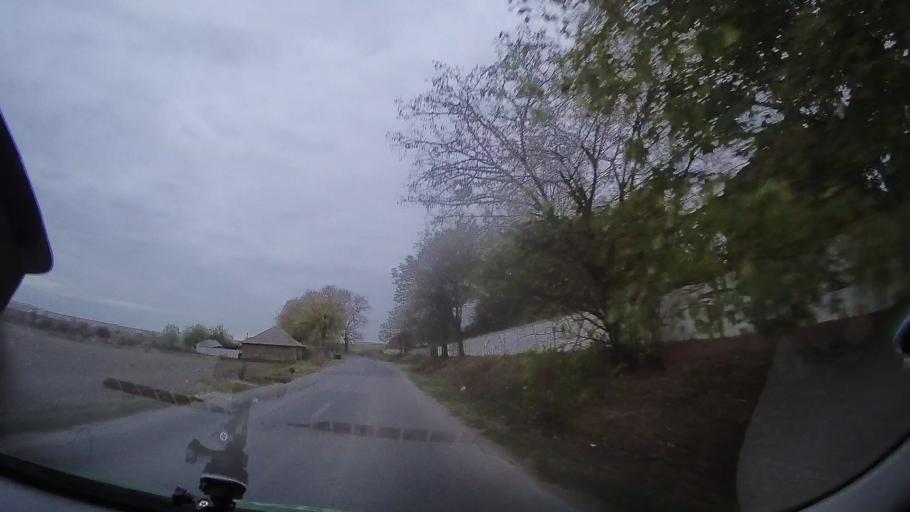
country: RO
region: Tulcea
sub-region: Comuna Mihai Bravu
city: Turda
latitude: 44.9680
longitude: 28.6299
